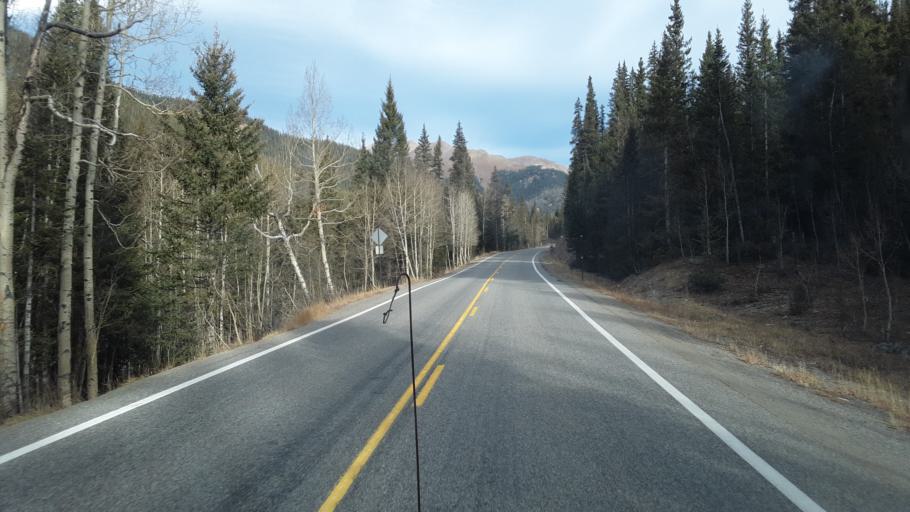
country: US
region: Colorado
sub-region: San Juan County
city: Silverton
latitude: 37.8236
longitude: -107.7198
